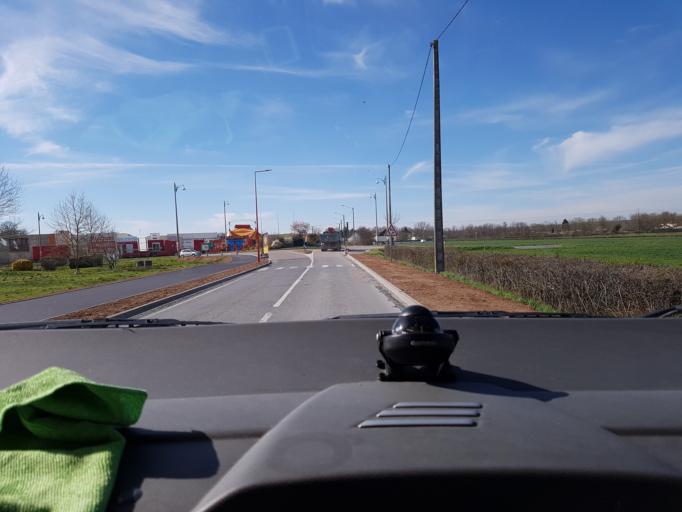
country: FR
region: Bourgogne
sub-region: Departement de Saone-et-Loire
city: Gueugnon
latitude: 46.5913
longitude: 4.0653
